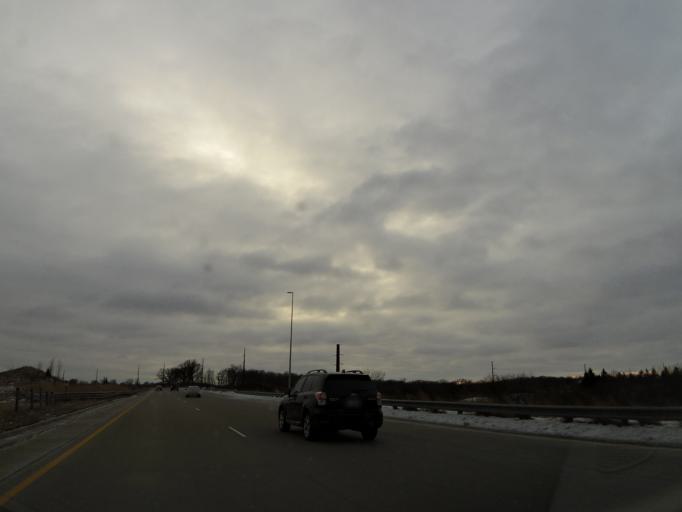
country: US
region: Minnesota
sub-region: Carver County
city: Chaska
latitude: 44.8018
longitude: -93.6289
